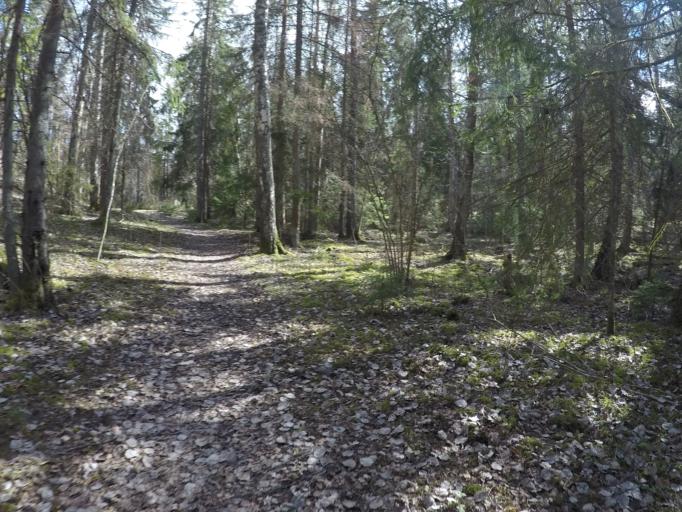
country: SE
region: Soedermanland
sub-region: Eskilstuna Kommun
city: Kvicksund
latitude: 59.4664
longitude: 16.3199
